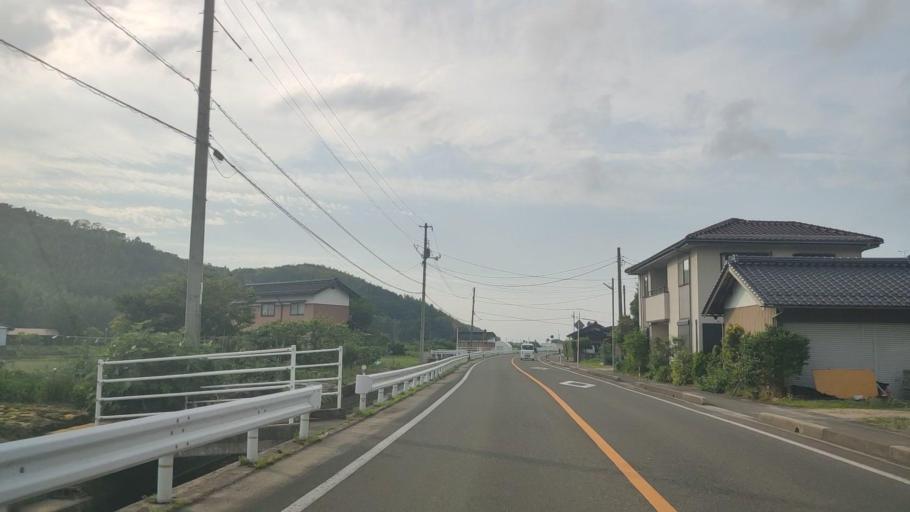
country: JP
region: Tottori
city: Kurayoshi
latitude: 35.4635
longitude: 133.8330
